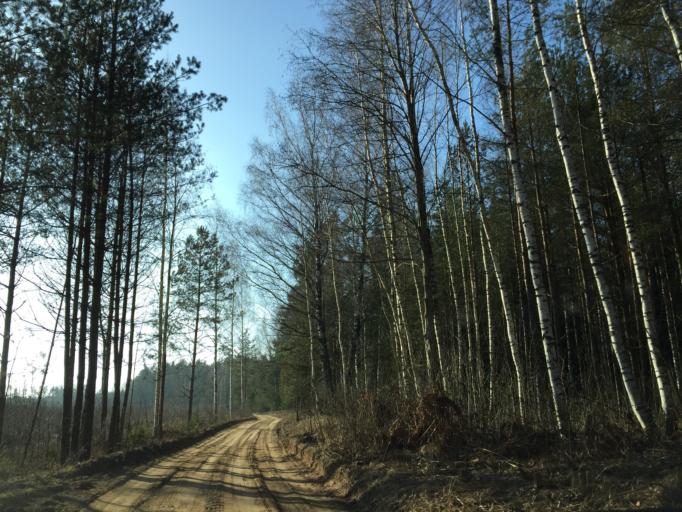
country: LV
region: Lecava
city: Iecava
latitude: 56.6764
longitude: 24.1949
